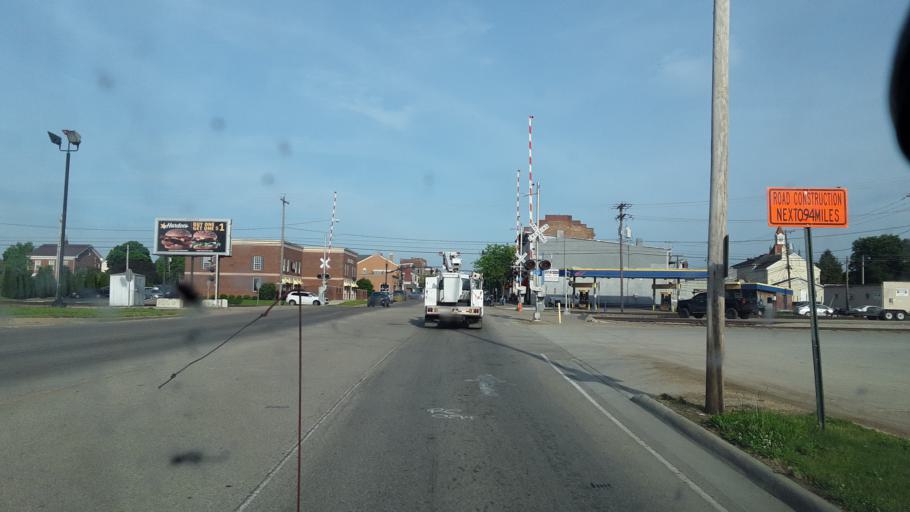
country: US
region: Ohio
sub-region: Pickaway County
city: Circleville
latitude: 39.6032
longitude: -82.9494
